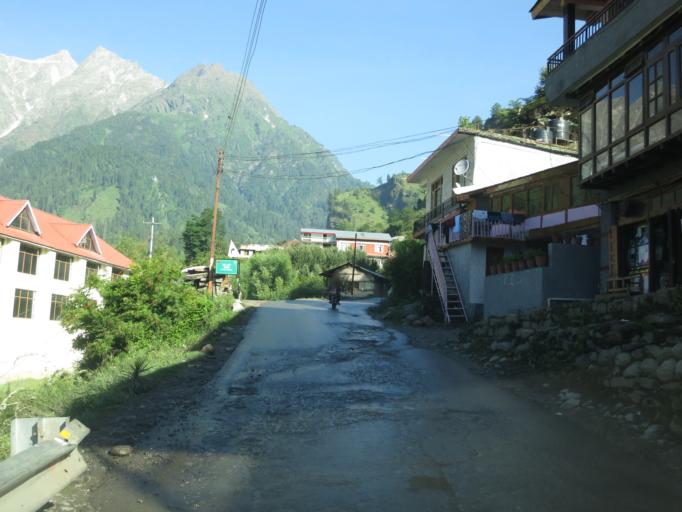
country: IN
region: Himachal Pradesh
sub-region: Kulu
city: Manali
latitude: 32.3091
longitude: 77.1757
